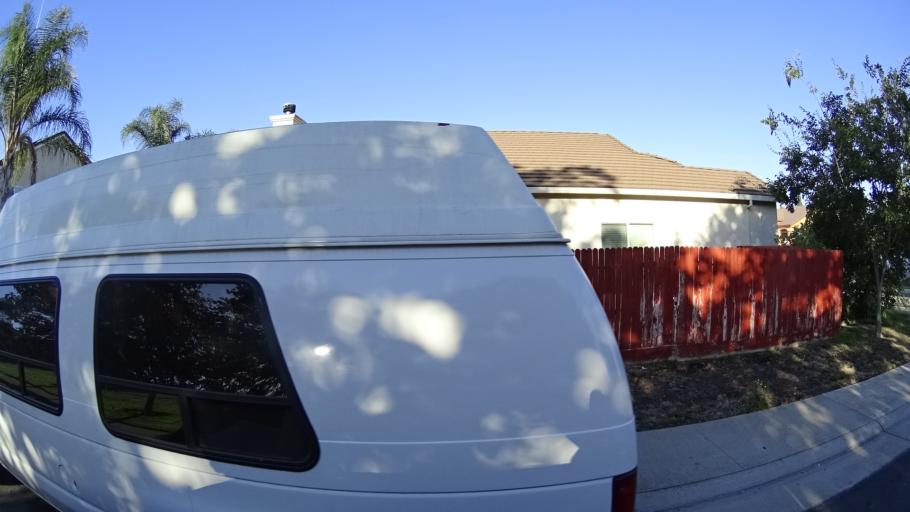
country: US
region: California
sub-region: Sacramento County
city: Laguna
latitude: 38.4301
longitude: -121.4545
